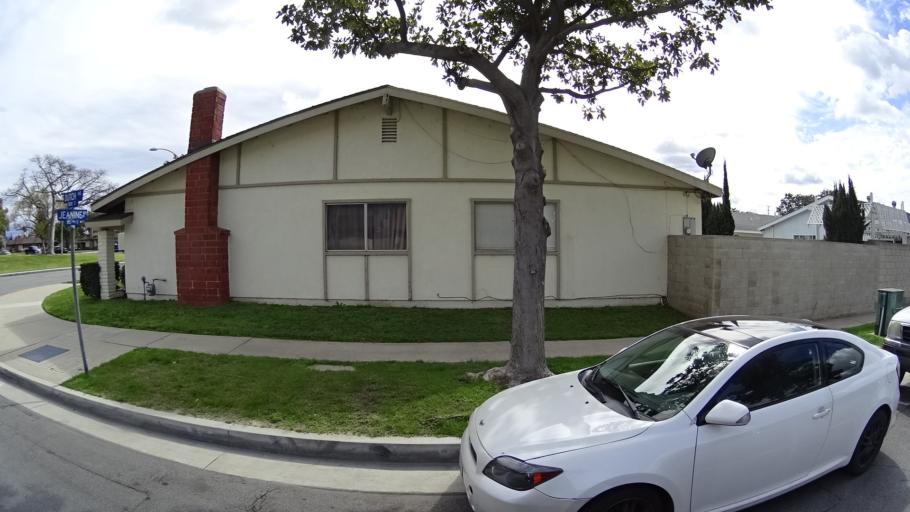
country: US
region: California
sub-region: Orange County
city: Placentia
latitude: 33.8424
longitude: -117.8698
